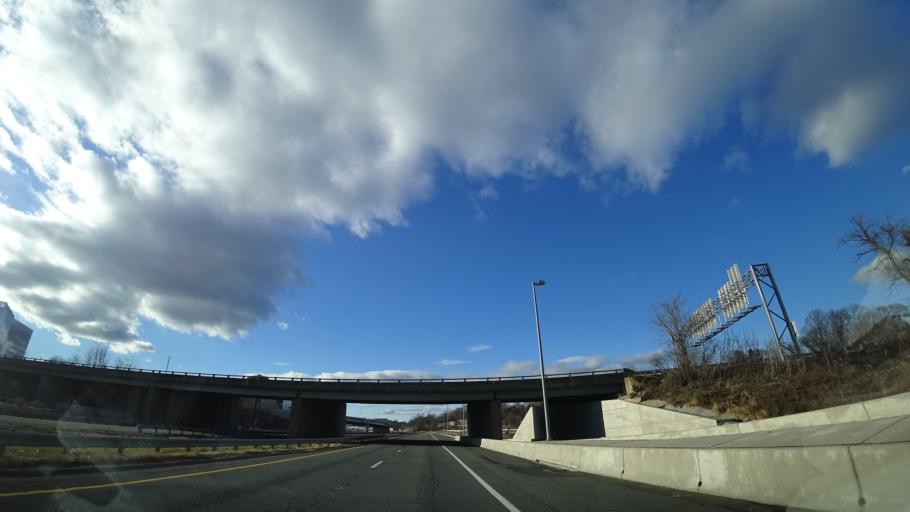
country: US
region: Virginia
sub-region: Fairfax County
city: Pimmit Hills
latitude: 38.9322
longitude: -77.2123
